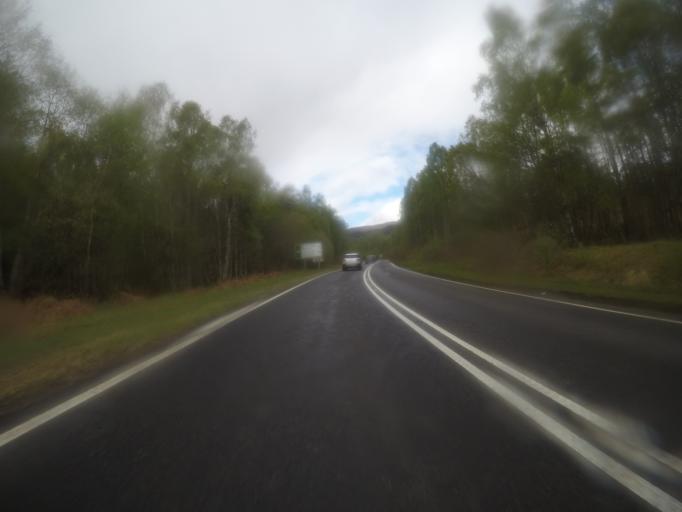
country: GB
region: Scotland
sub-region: Highland
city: Spean Bridge
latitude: 57.0824
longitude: -4.8983
